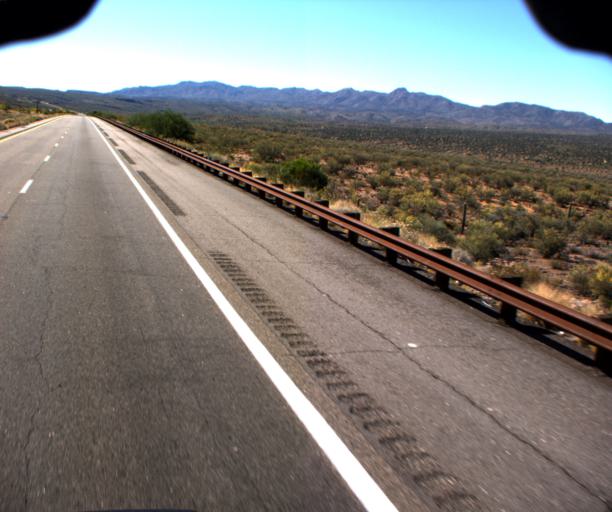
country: US
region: Arizona
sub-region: Yavapai County
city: Bagdad
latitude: 34.5275
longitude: -113.4284
